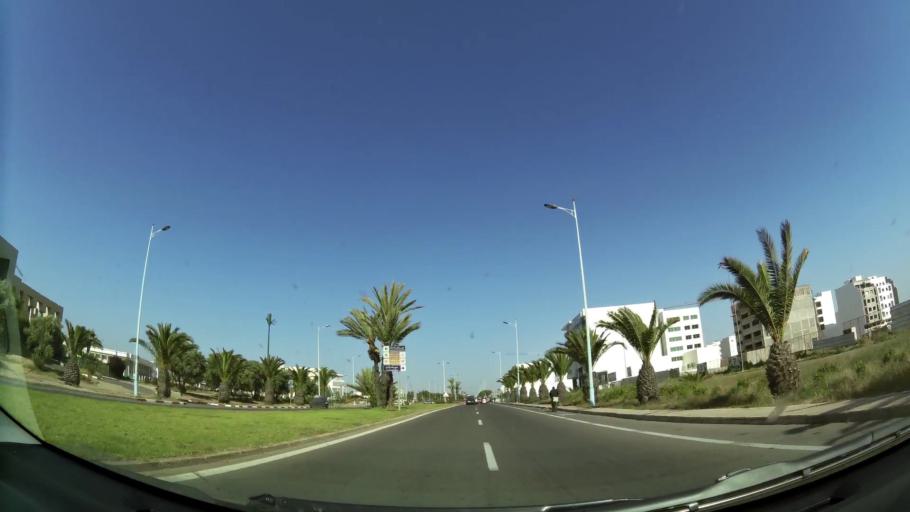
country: MA
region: Souss-Massa-Draa
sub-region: Agadir-Ida-ou-Tnan
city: Agadir
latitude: 30.4031
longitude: -9.5798
